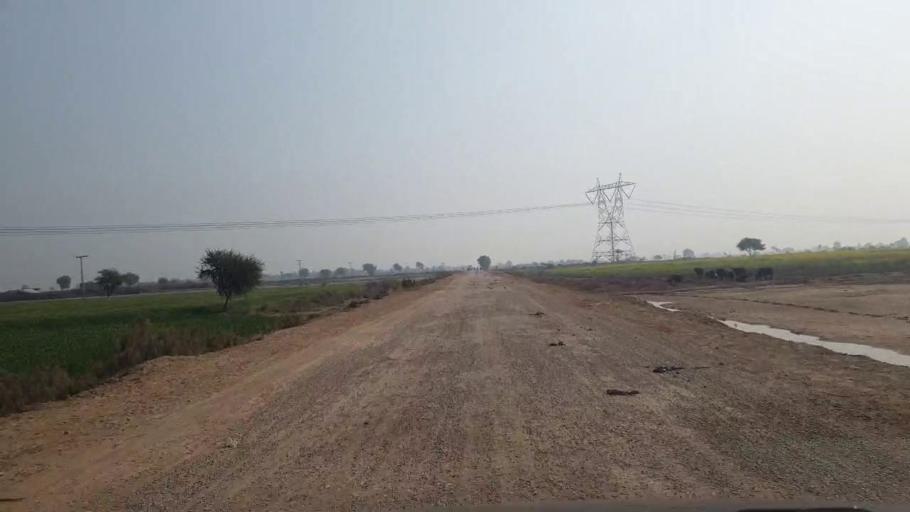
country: PK
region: Sindh
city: Hala
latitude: 25.9415
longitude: 68.4448
